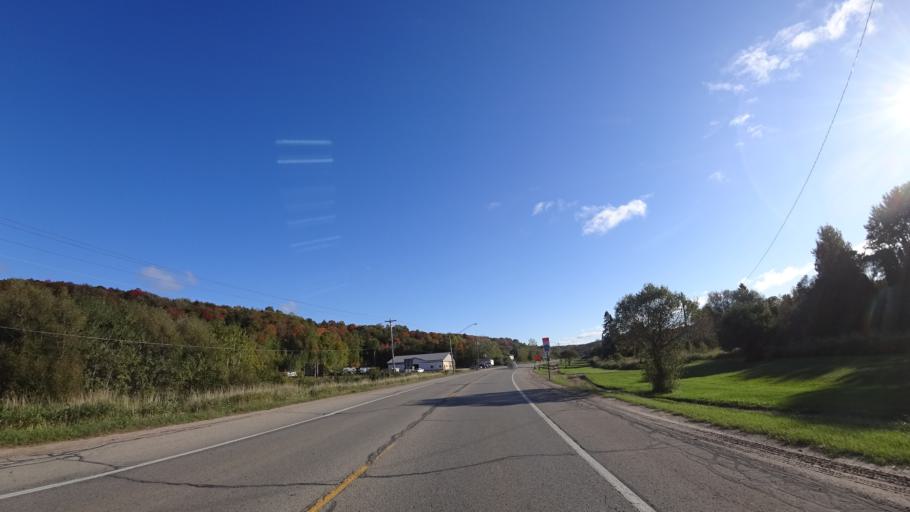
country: US
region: Michigan
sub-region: Alger County
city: Munising
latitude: 46.4020
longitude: -86.6478
